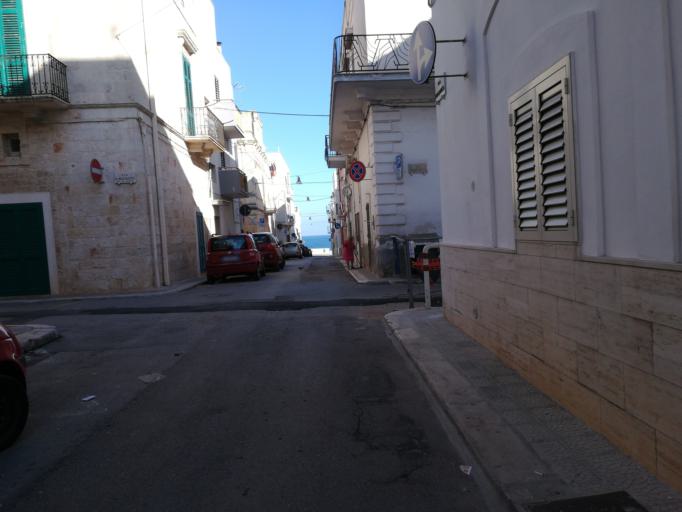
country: IT
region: Apulia
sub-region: Provincia di Bari
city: Polignano a Mare
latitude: 40.9951
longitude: 17.2244
